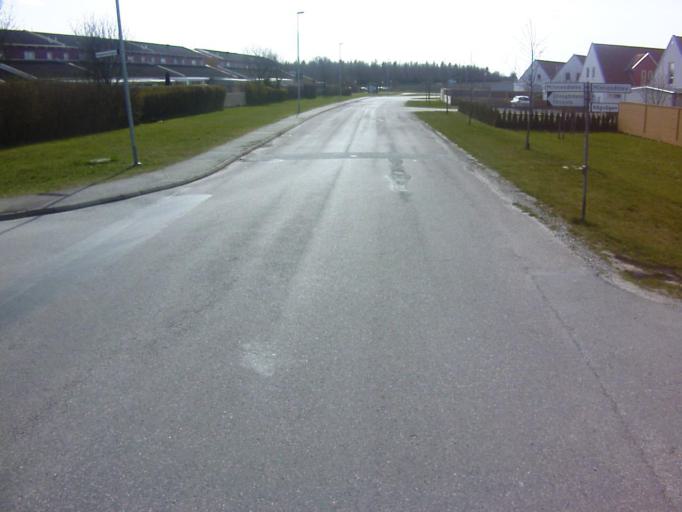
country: SE
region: Skane
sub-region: Kavlinge Kommun
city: Kaevlinge
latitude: 55.8040
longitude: 13.1029
